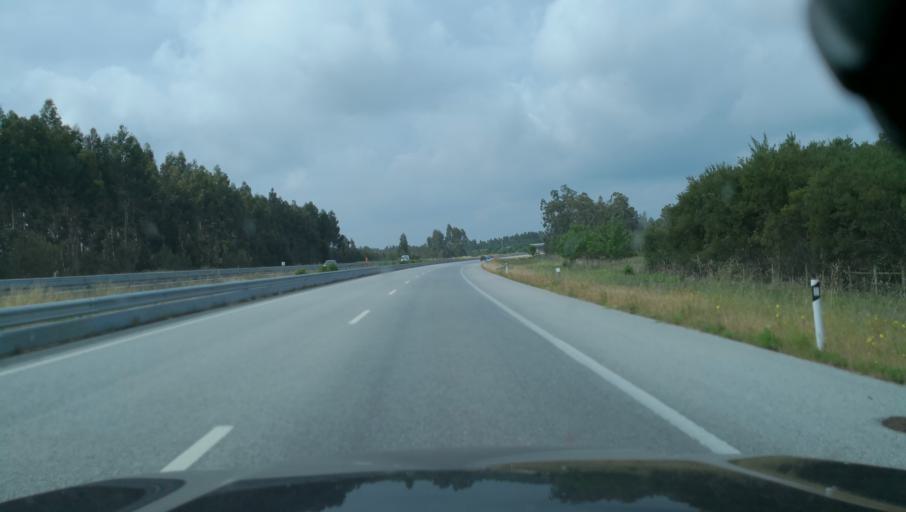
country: PT
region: Coimbra
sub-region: Montemor-O-Velho
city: Arazede
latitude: 40.2902
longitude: -8.7433
